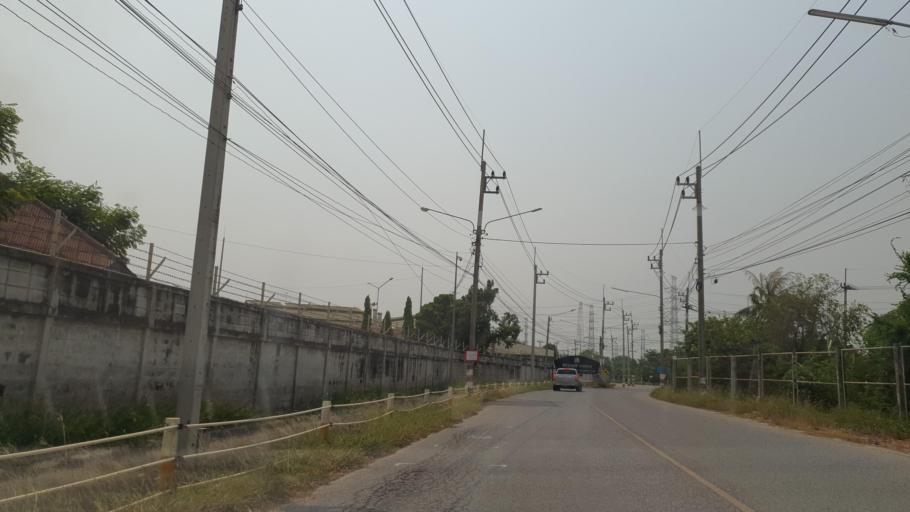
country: TH
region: Chachoengsao
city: Bang Pakong
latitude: 13.5055
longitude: 101.0325
